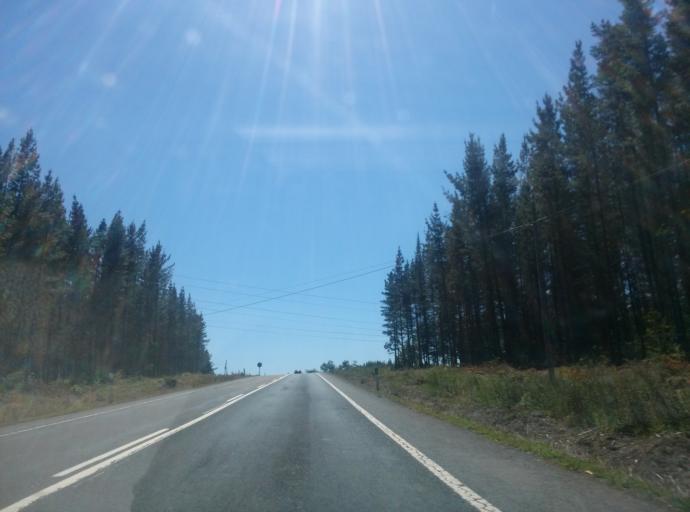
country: ES
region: Galicia
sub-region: Provincia de Lugo
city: Castro de Rei
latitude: 43.1326
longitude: -7.4141
